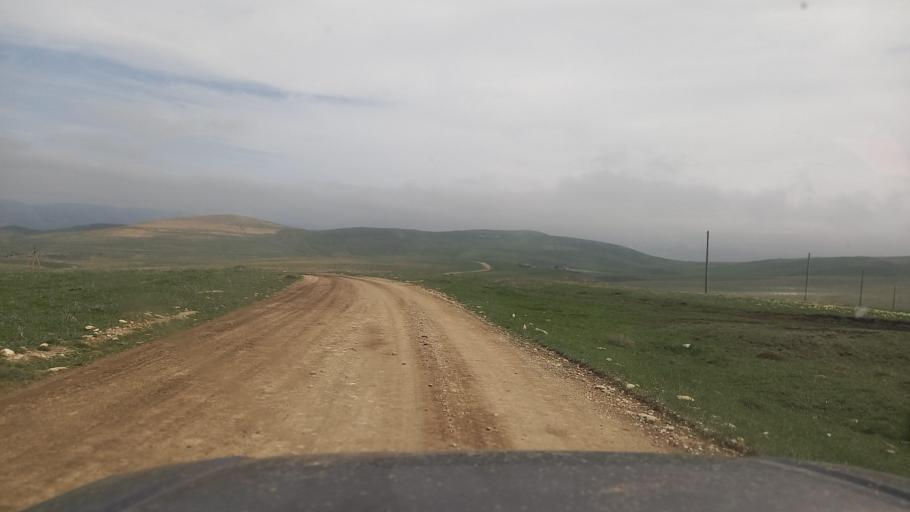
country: RU
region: Stavropol'skiy
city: Kislovodsk
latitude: 43.7688
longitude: 42.8390
